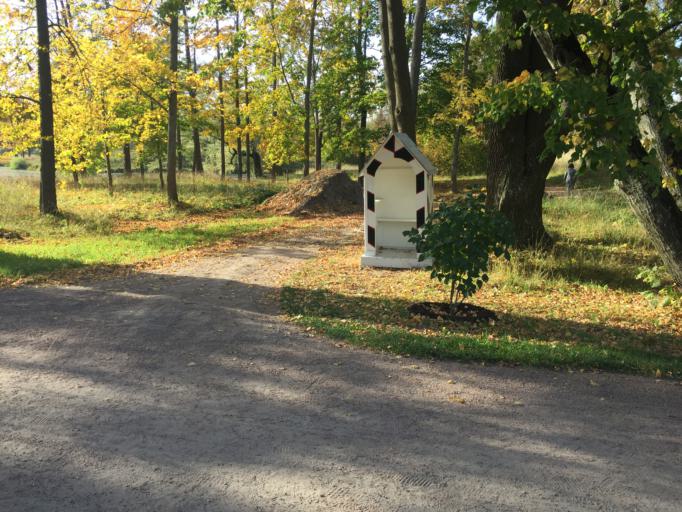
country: RU
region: St.-Petersburg
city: Pushkin
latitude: 59.7144
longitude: 30.3803
